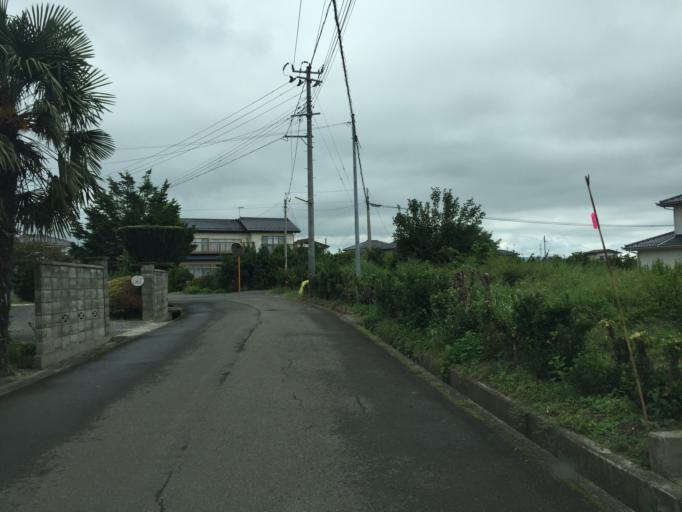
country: JP
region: Fukushima
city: Fukushima-shi
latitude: 37.7652
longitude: 140.3942
